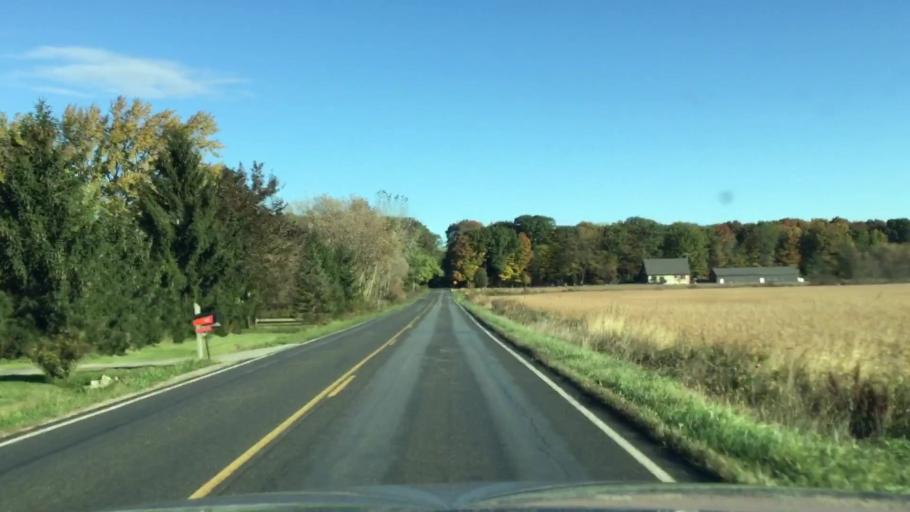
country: US
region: Michigan
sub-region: Shiawassee County
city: Durand
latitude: 42.9281
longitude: -83.9488
